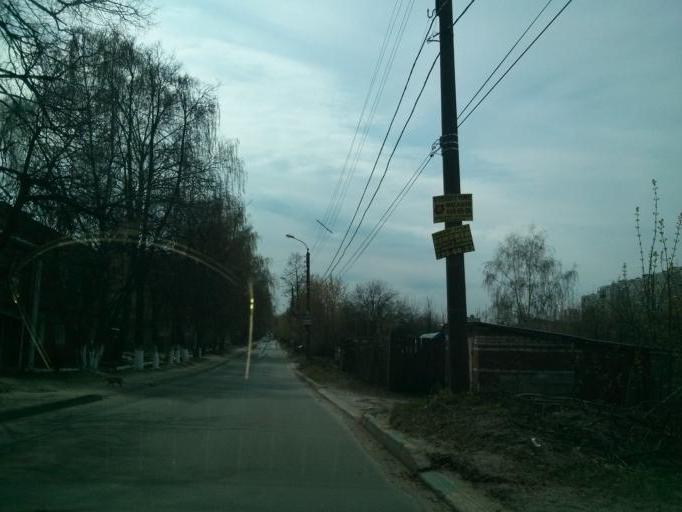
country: RU
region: Nizjnij Novgorod
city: Bor
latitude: 56.3128
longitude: 44.0541
